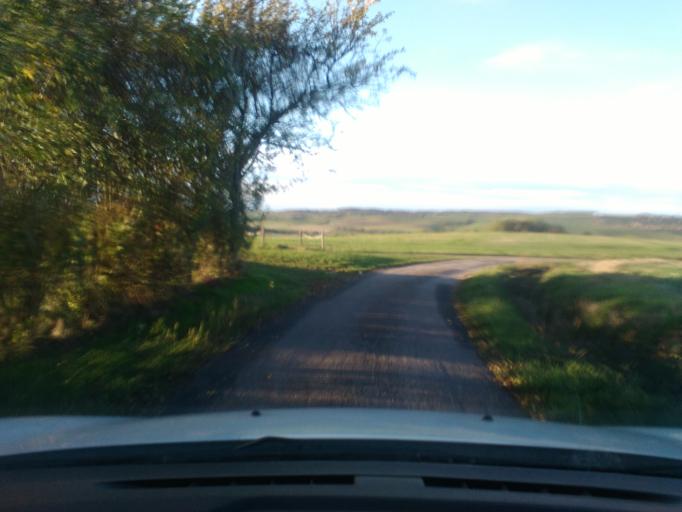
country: FR
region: Lorraine
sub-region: Departement des Vosges
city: Charmes
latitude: 48.3436
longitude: 6.2517
